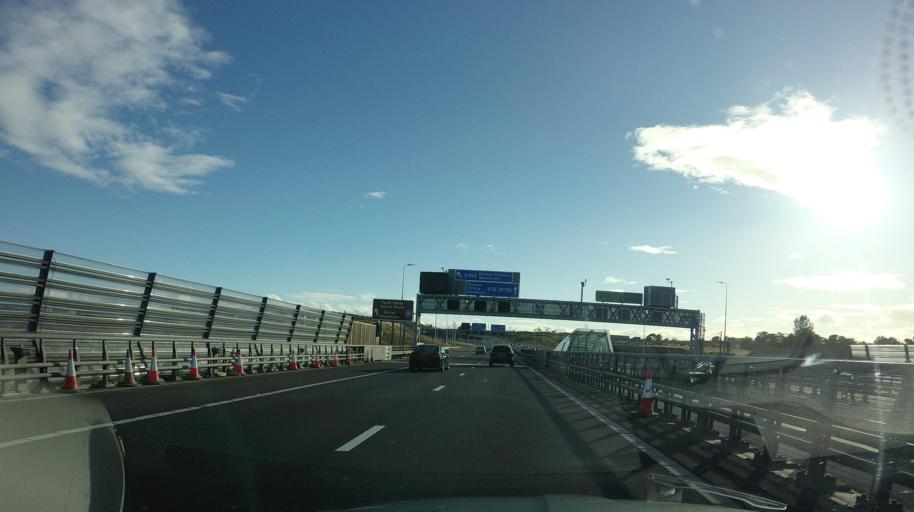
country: GB
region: Scotland
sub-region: Edinburgh
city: Queensferry
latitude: 55.9917
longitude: -3.4205
